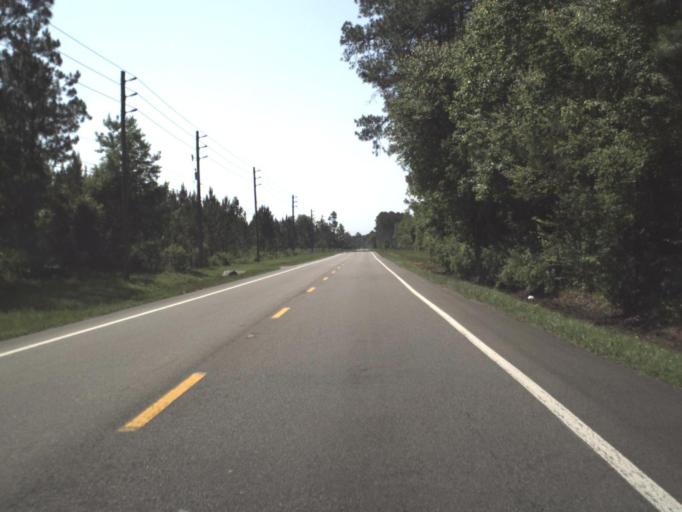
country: US
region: Florida
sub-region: Nassau County
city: Nassau Village-Ratliff
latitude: 30.4985
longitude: -81.7444
